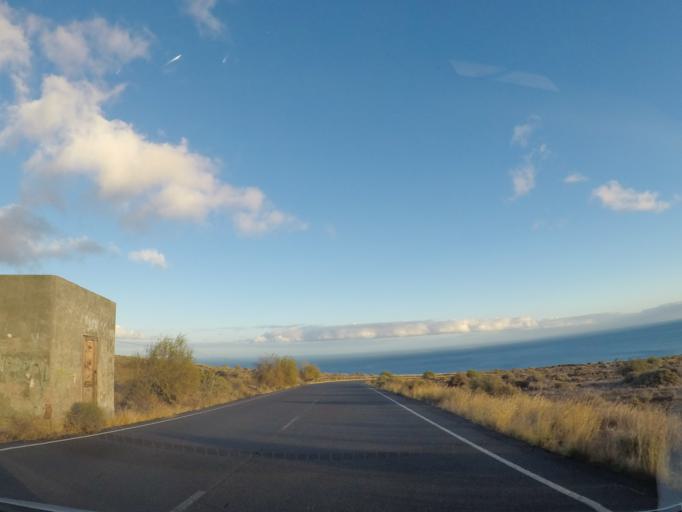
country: ES
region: Canary Islands
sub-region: Provincia de Santa Cruz de Tenerife
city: Alajero
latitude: 28.0371
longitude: -17.2202
